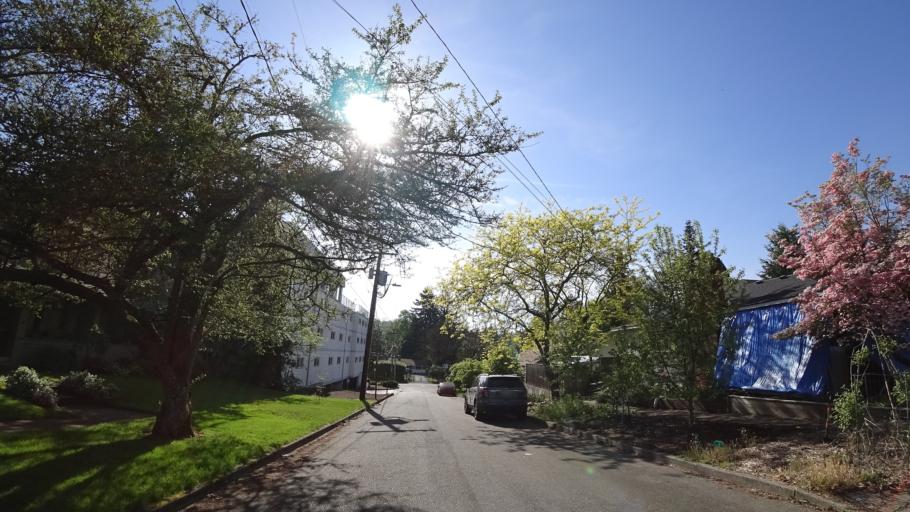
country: US
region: Oregon
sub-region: Clackamas County
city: Milwaukie
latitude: 45.4471
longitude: -122.6383
